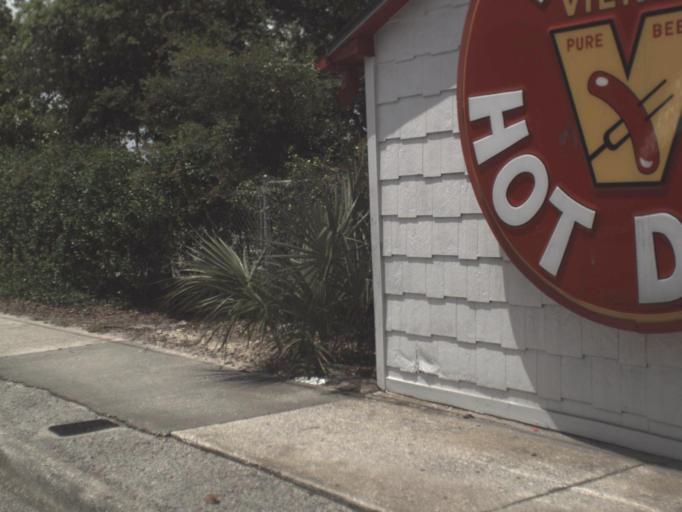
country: US
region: Florida
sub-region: Hillsborough County
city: Temple Terrace
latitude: 28.0327
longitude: -82.4125
